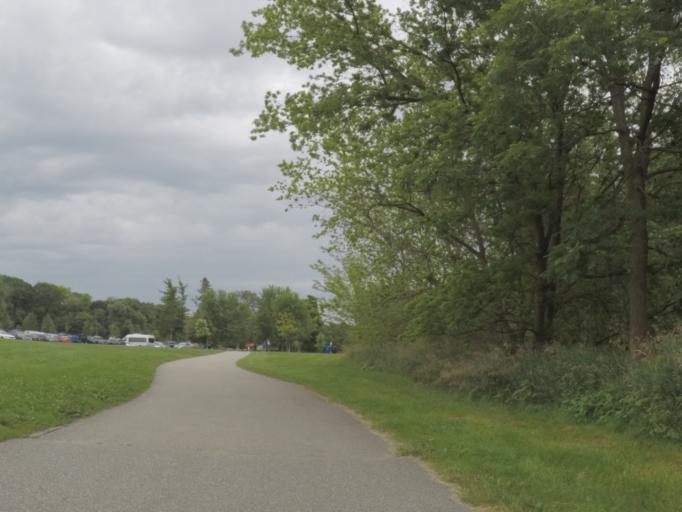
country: CA
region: Ontario
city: Etobicoke
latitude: 43.6619
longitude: -79.5596
